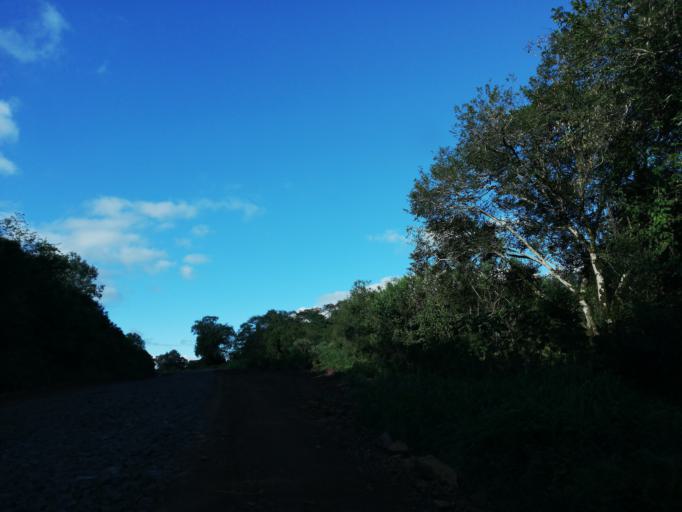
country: AR
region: Misiones
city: Almafuerte
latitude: -27.5513
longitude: -55.4166
